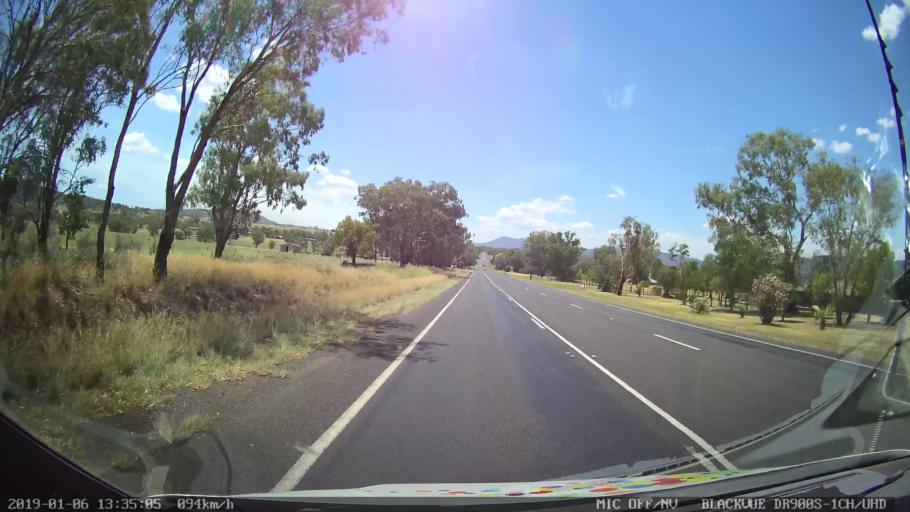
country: AU
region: New South Wales
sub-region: Tamworth Municipality
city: Kootingal
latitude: -31.0813
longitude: 151.0218
